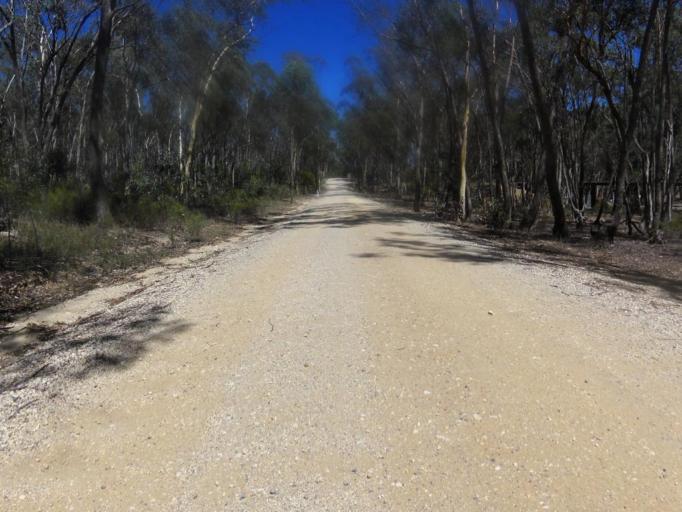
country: AU
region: Victoria
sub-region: Mount Alexander
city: Castlemaine
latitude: -37.0455
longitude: 144.1818
